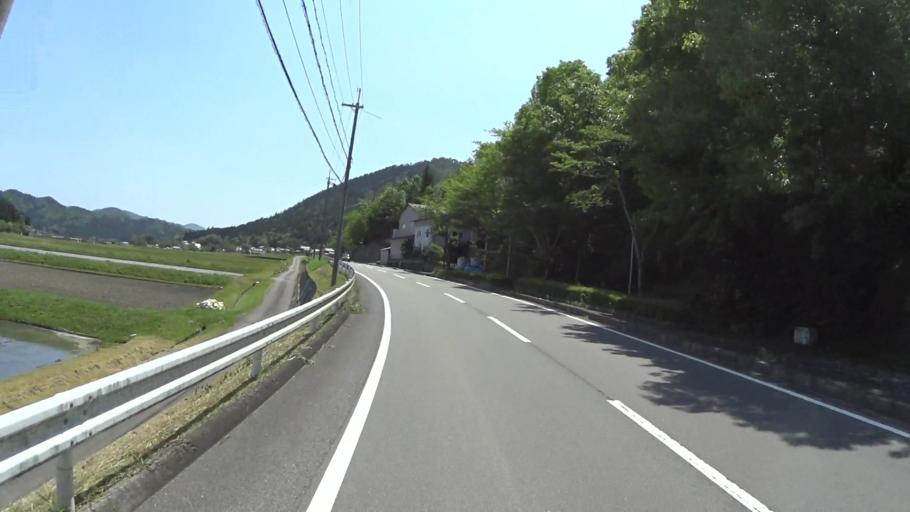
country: JP
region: Kyoto
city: Kameoka
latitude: 35.0310
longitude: 135.4842
